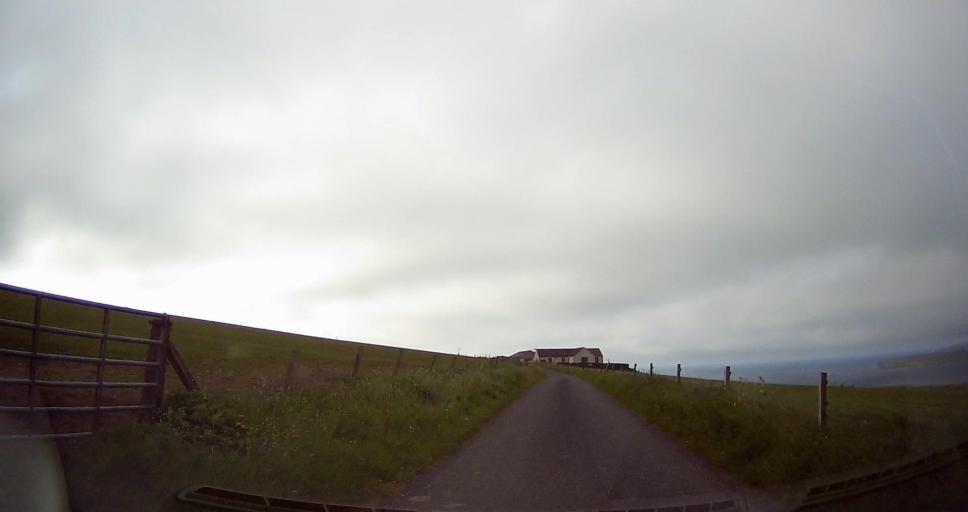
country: GB
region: Scotland
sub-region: Orkney Islands
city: Orkney
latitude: 59.1187
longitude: -3.1323
